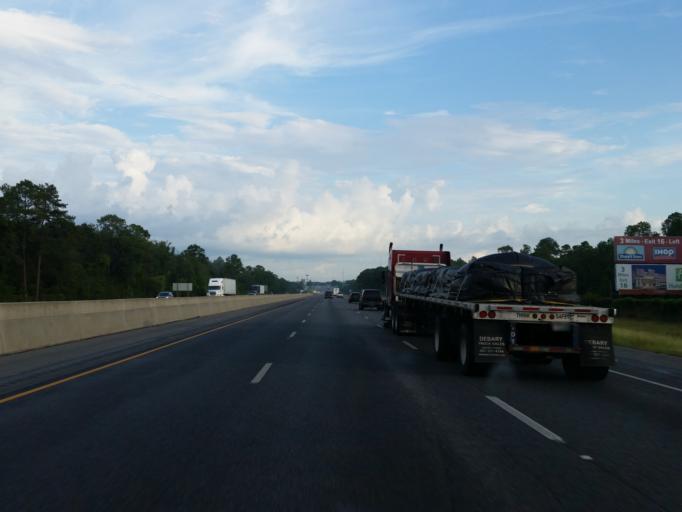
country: US
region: Georgia
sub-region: Lowndes County
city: Remerton
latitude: 30.8671
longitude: -83.3387
